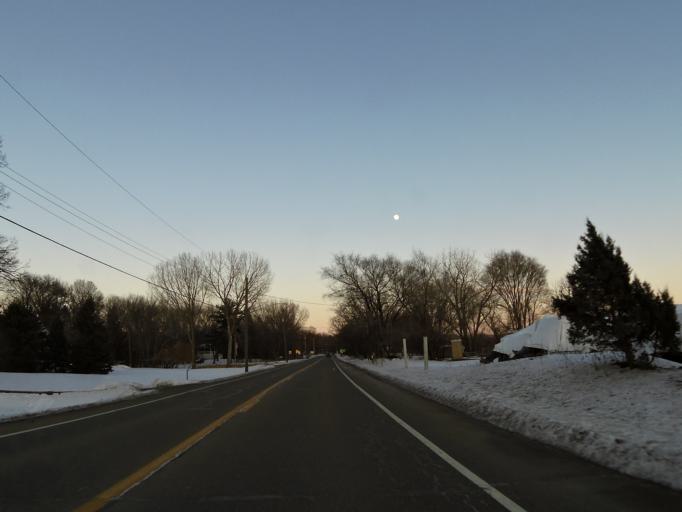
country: US
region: Minnesota
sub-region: Ramsey County
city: White Bear Lake
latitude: 45.0970
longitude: -92.9948
